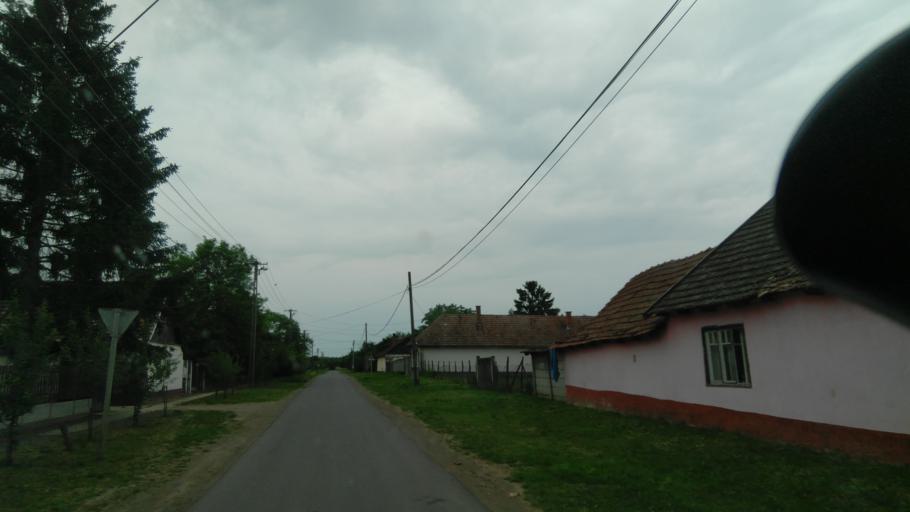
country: HU
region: Bekes
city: Doboz
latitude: 46.7282
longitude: 21.2466
